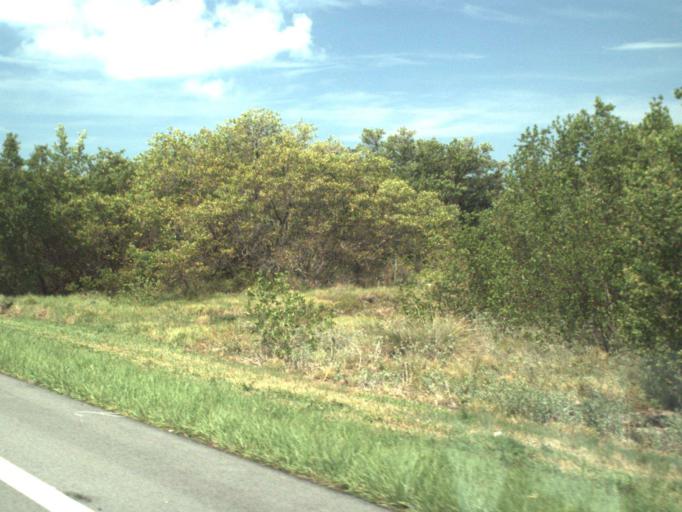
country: US
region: Florida
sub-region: Monroe County
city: Islamorada
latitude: 24.8352
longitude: -80.8018
